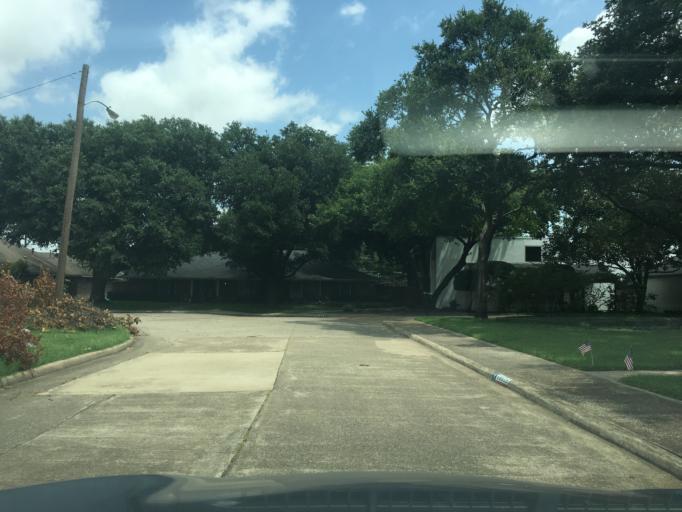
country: US
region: Texas
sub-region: Dallas County
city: Addison
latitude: 32.9124
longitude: -96.8218
